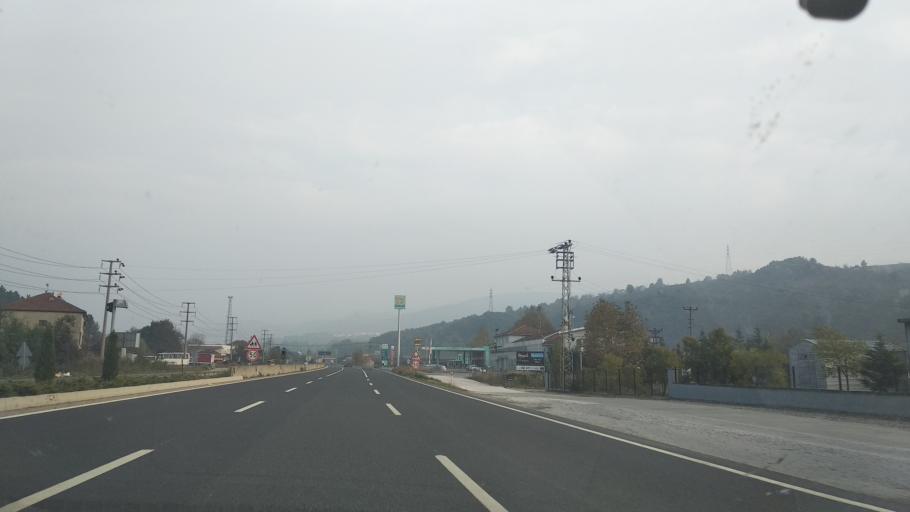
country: TR
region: Duzce
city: Kaynasli
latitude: 40.7890
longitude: 31.2598
